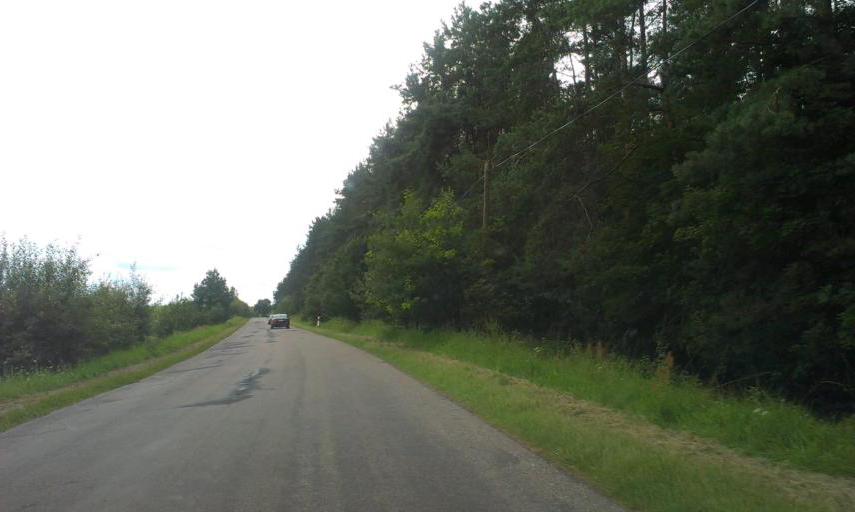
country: PL
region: West Pomeranian Voivodeship
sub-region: Powiat szczecinecki
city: Barwice
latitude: 53.6892
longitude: 16.3432
